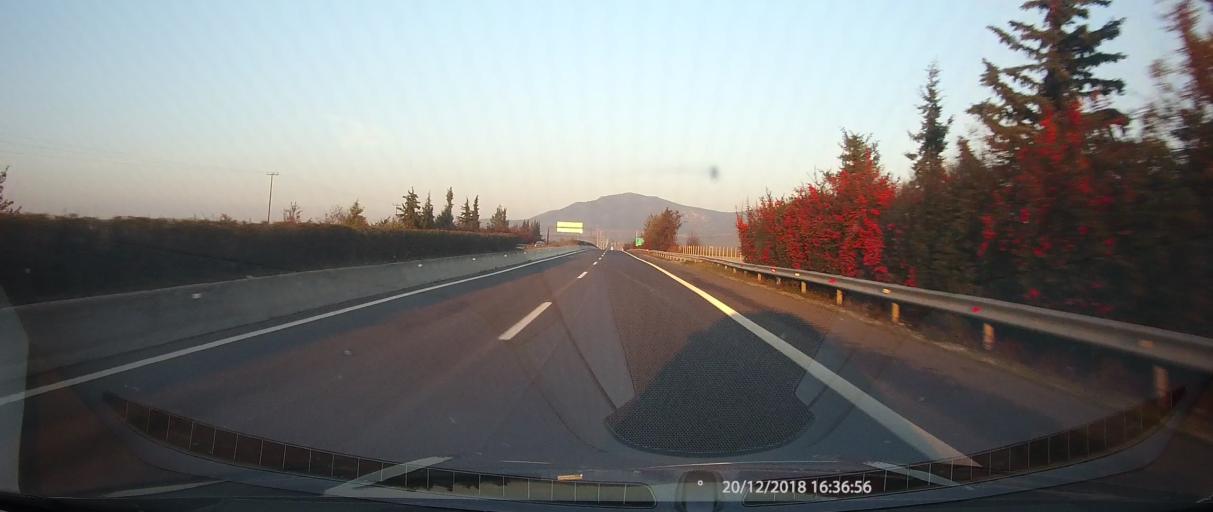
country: GR
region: Thessaly
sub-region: Nomos Magnisias
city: Velestino
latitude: 39.3217
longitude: 22.7664
